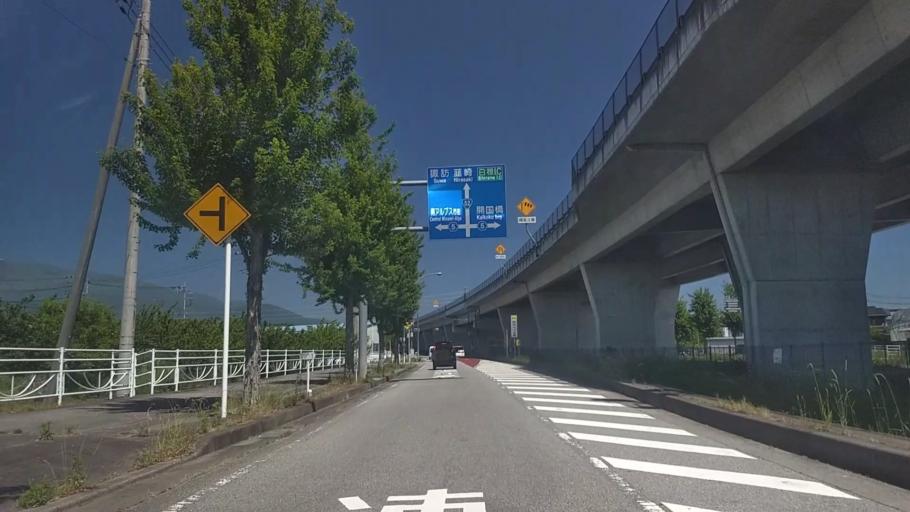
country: JP
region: Yamanashi
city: Ryuo
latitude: 35.6188
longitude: 138.4788
